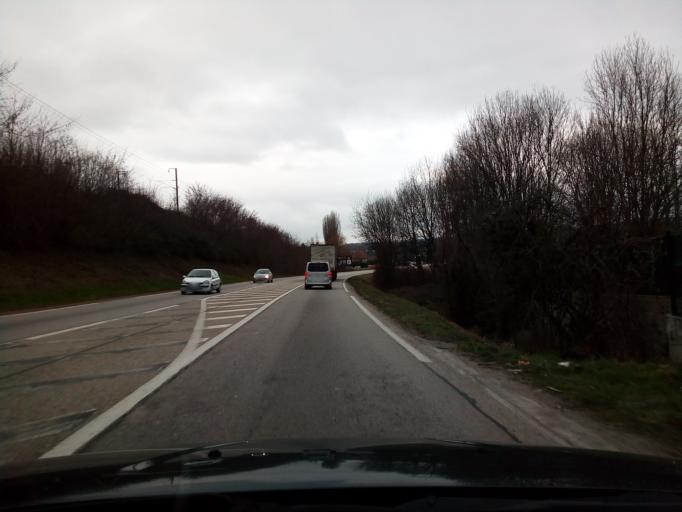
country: FR
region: Rhone-Alpes
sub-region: Departement de l'Isere
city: Moirans
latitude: 45.3274
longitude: 5.5726
